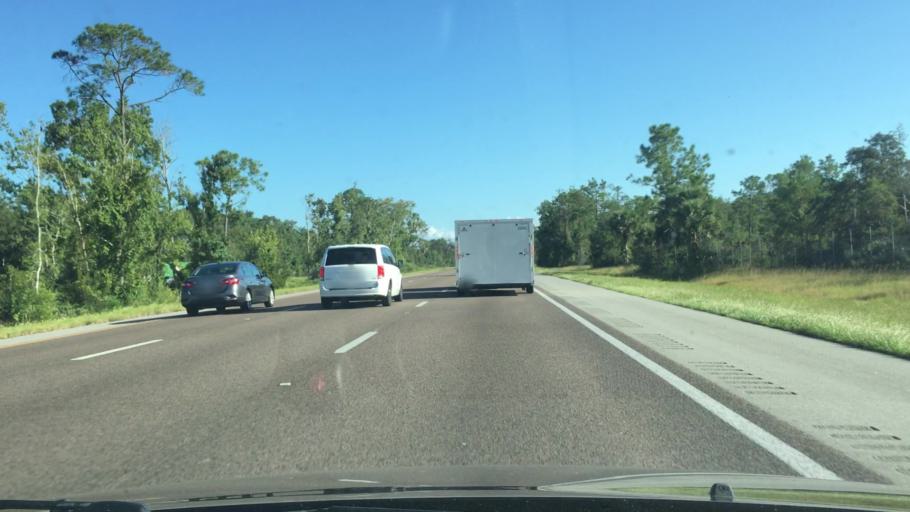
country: US
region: Florida
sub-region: Volusia County
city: Edgewater
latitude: 28.9332
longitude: -80.9429
